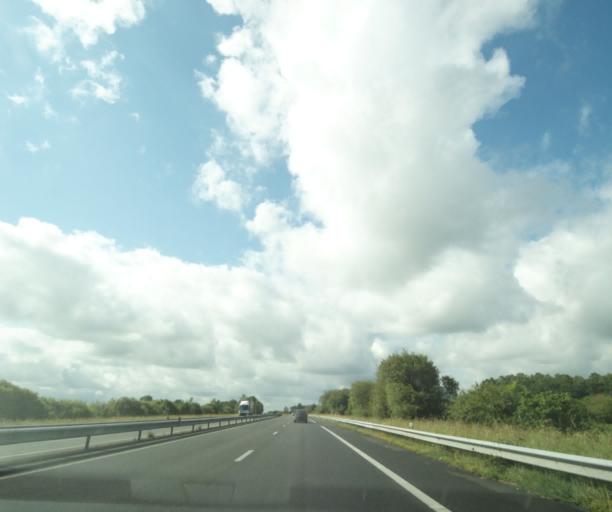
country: FR
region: Pays de la Loire
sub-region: Departement de Maine-et-Loire
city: Durtal
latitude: 47.7207
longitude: -0.2513
